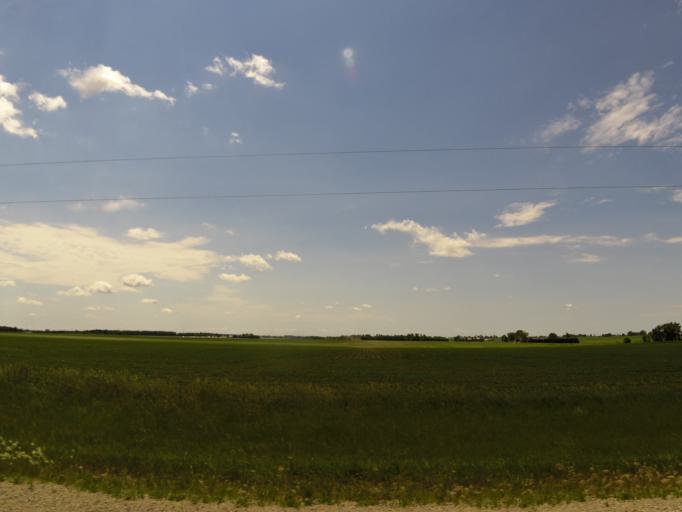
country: US
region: Iowa
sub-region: Buchanan County
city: Fairbank
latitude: 42.7149
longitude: -92.0581
